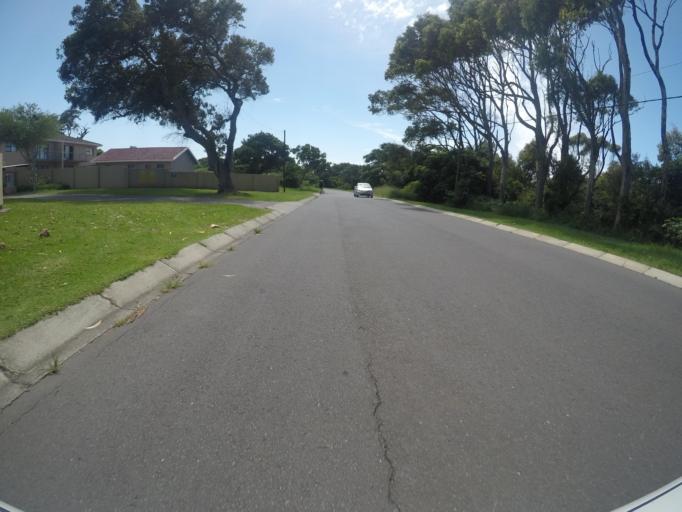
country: ZA
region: Eastern Cape
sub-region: Buffalo City Metropolitan Municipality
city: East London
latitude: -32.9492
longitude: 28.0006
